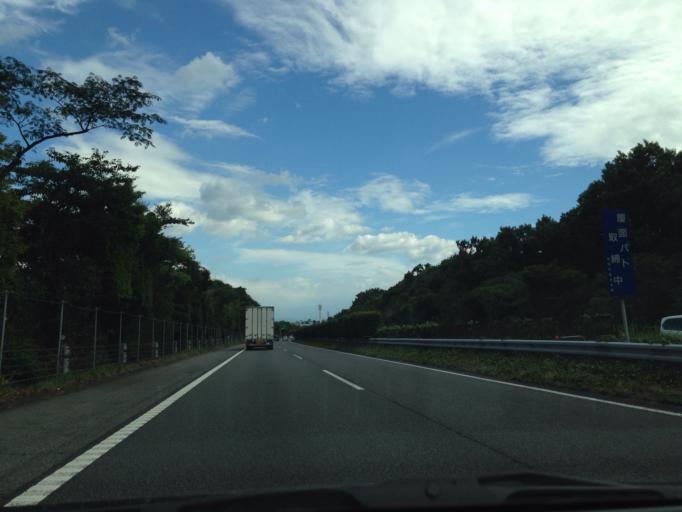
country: JP
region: Shizuoka
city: Gotemba
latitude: 35.2327
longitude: 138.9099
